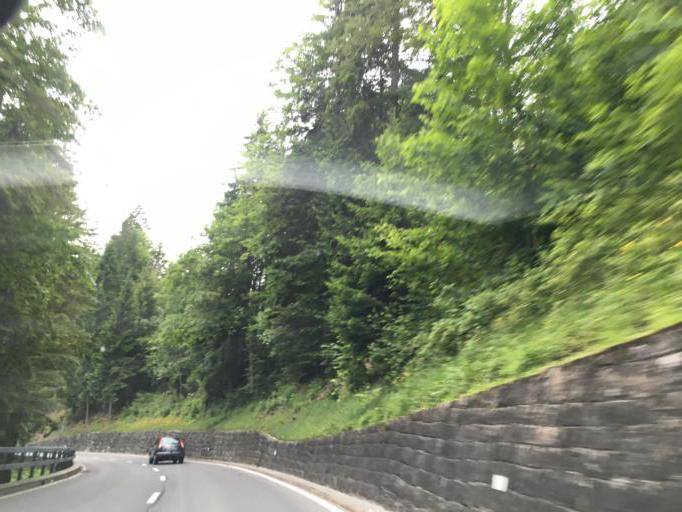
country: CH
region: Obwalden
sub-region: Obwalden
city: Engelberg
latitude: 46.8273
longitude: 8.3803
